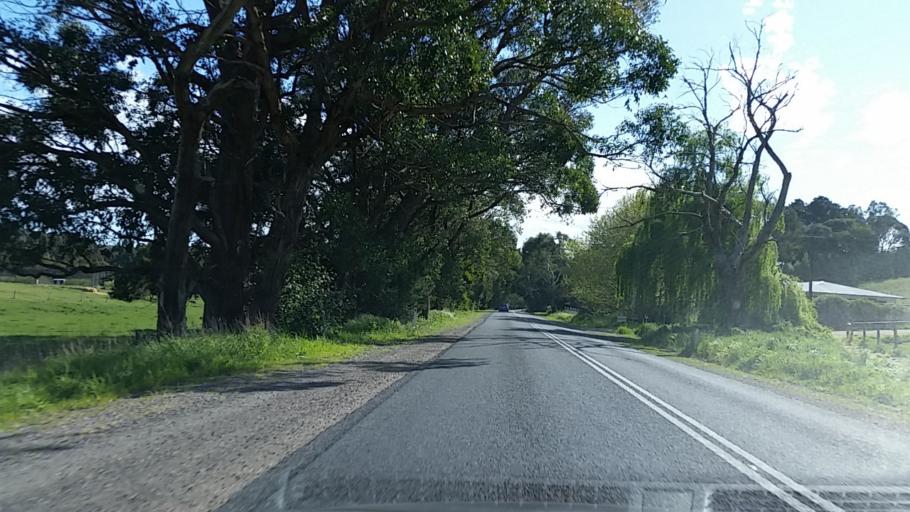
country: AU
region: South Australia
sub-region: Alexandrina
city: Mount Compass
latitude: -35.2673
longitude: 138.6396
